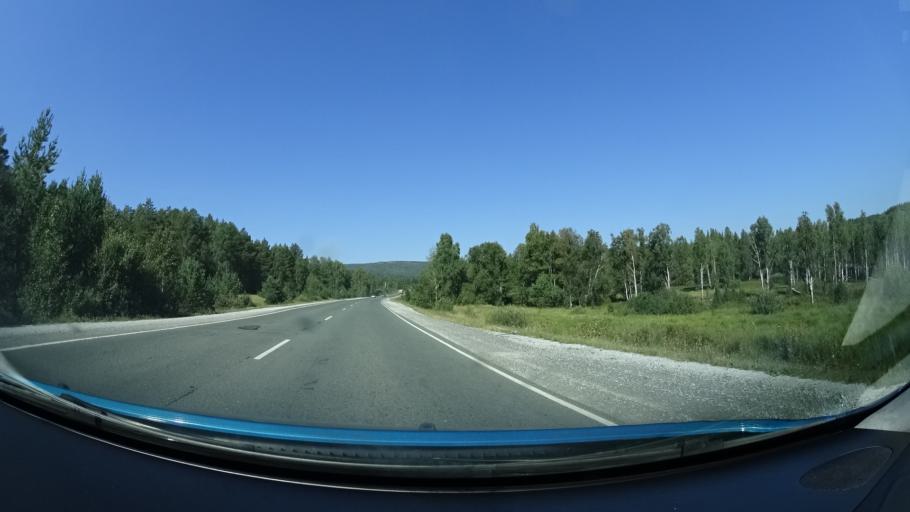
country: RU
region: Bashkortostan
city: Abzakovo
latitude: 53.8571
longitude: 58.5655
